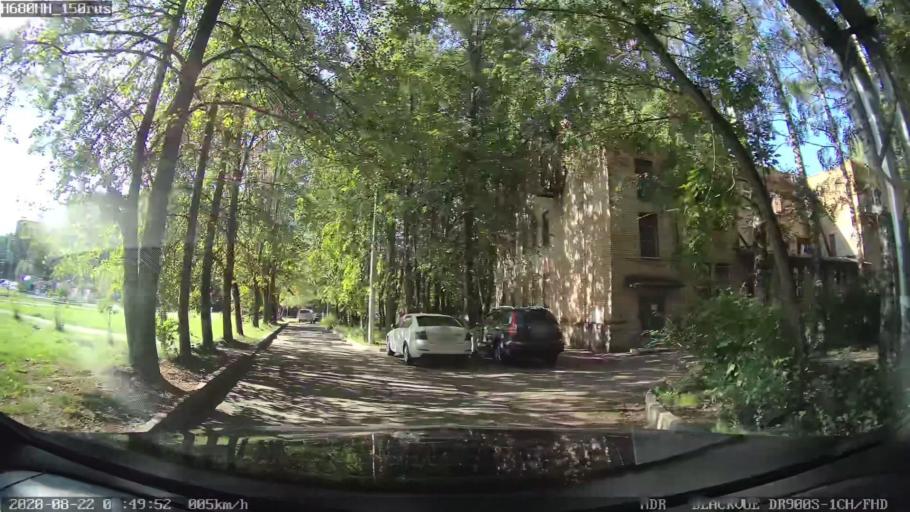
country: RU
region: Moskovskaya
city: Solnechnogorsk
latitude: 56.2165
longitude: 37.0262
